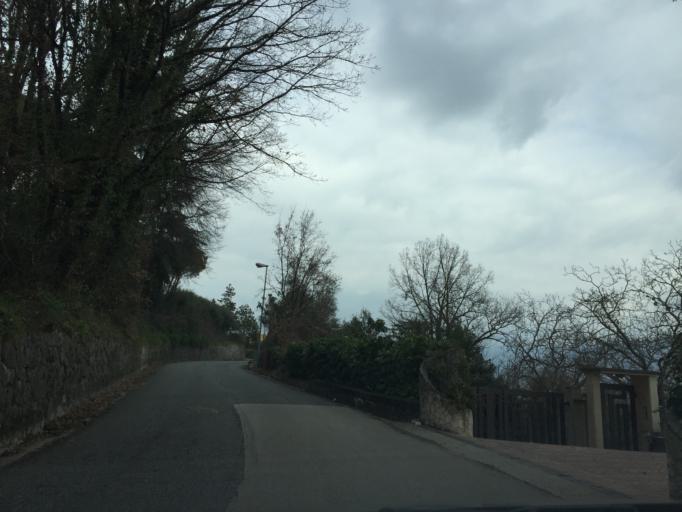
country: IT
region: Latium
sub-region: Provincia di Frosinone
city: Cassino
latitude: 41.4843
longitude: 13.8230
